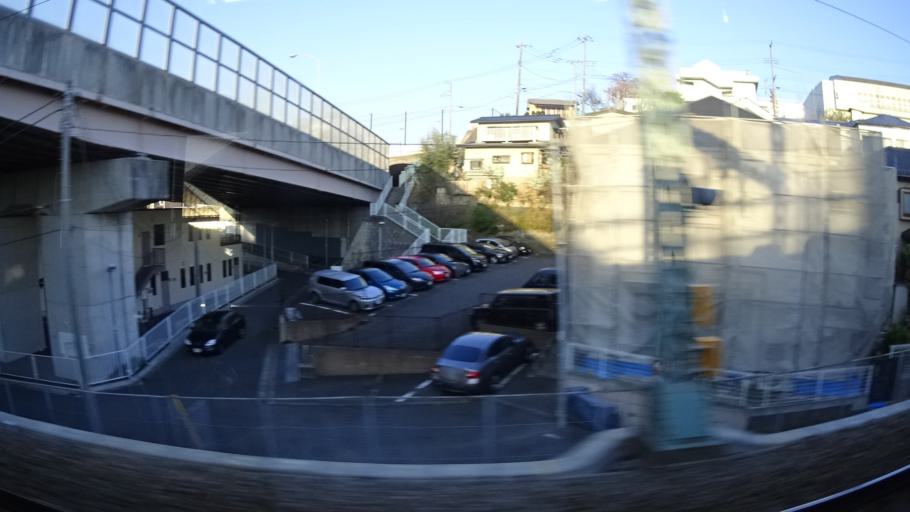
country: JP
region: Kanagawa
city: Yokohama
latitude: 35.3780
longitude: 139.6187
